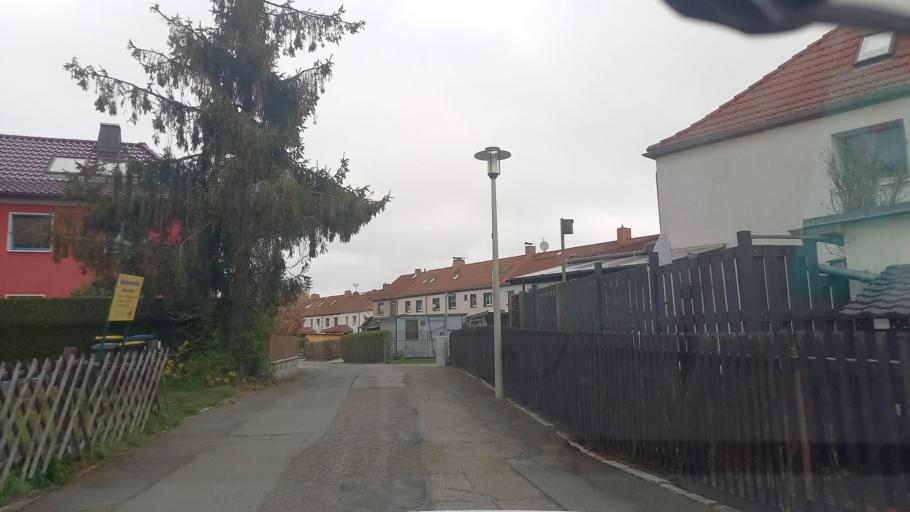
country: DE
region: Saxony
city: Zwickau
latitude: 50.6989
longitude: 12.4906
